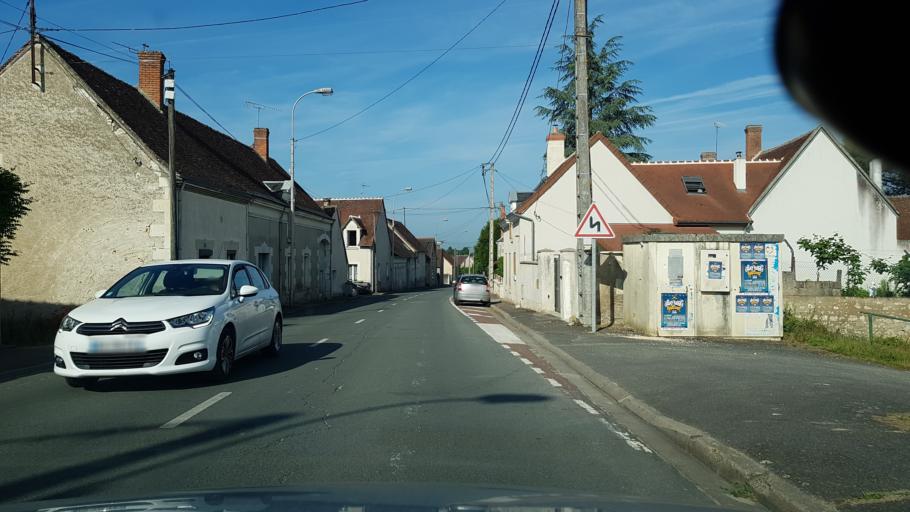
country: FR
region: Centre
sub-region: Departement du Loir-et-Cher
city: Selles-sur-Cher
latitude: 47.2806
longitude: 1.5655
